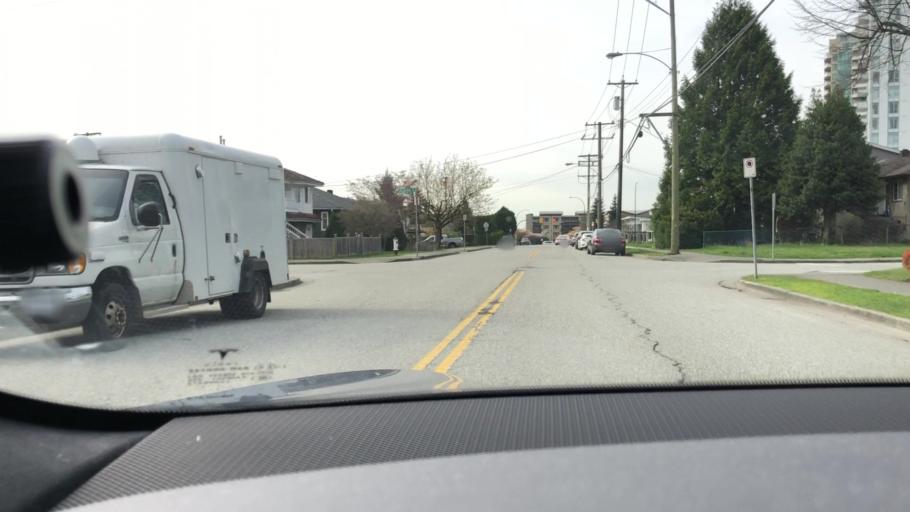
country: CA
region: British Columbia
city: Burnaby
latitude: 49.2206
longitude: -122.9648
